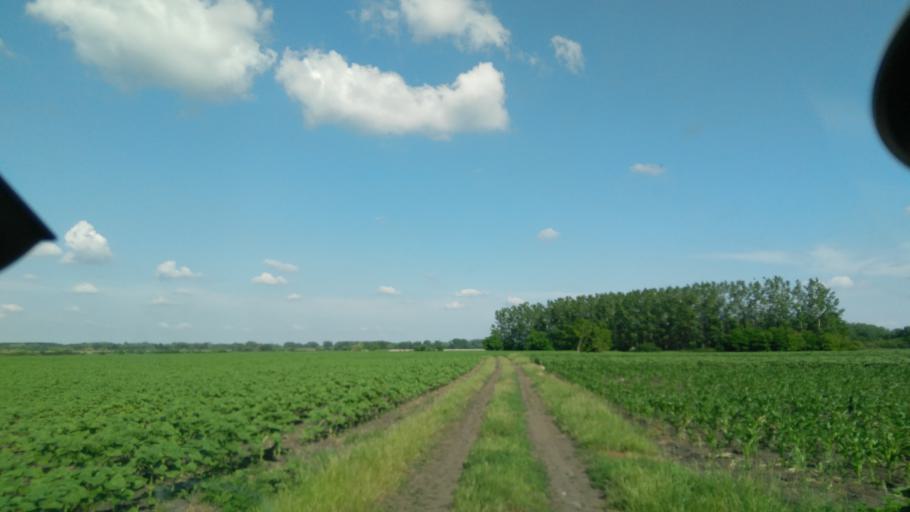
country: HU
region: Bekes
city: Doboz
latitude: 46.7019
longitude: 21.2358
